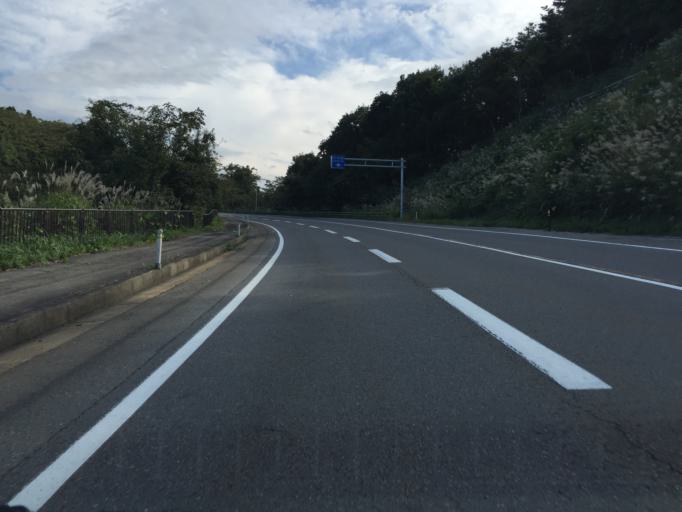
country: JP
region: Fukushima
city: Inawashiro
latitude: 37.5235
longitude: 139.9822
